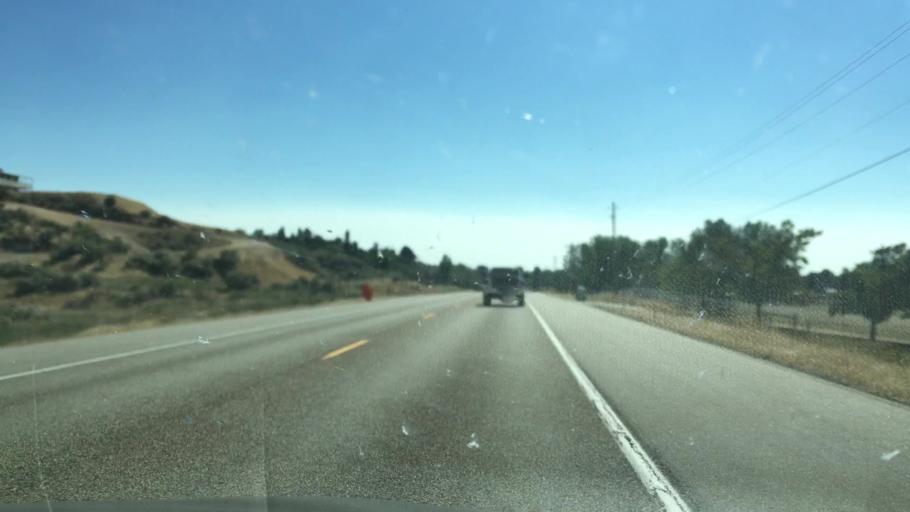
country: US
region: Idaho
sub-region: Ada County
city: Eagle
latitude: 43.7261
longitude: -116.3109
